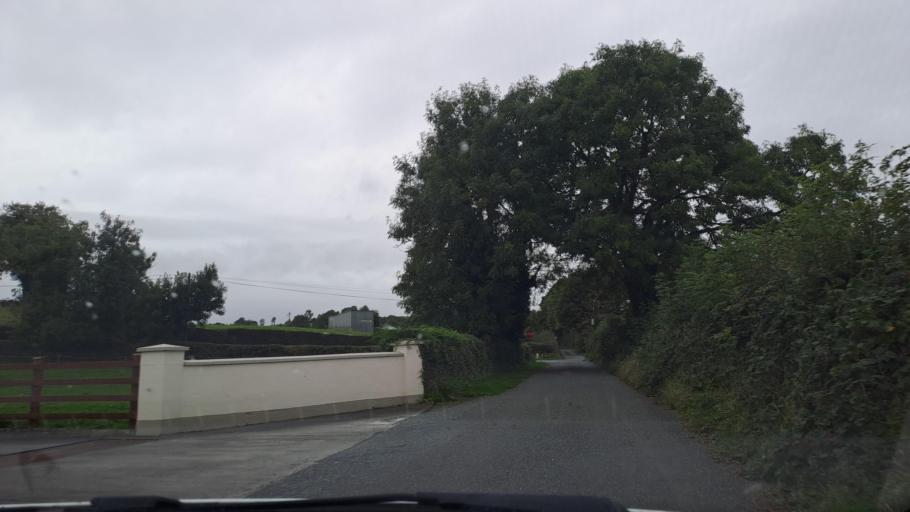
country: IE
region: Ulster
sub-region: County Monaghan
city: Carrickmacross
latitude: 53.9827
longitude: -6.7561
